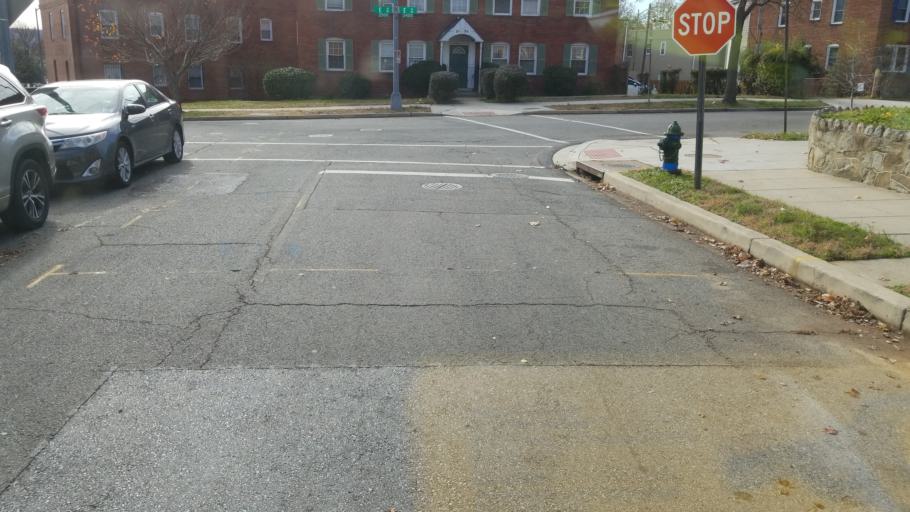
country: US
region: Maryland
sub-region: Prince George's County
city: Colmar Manor
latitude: 38.8963
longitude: -76.9718
